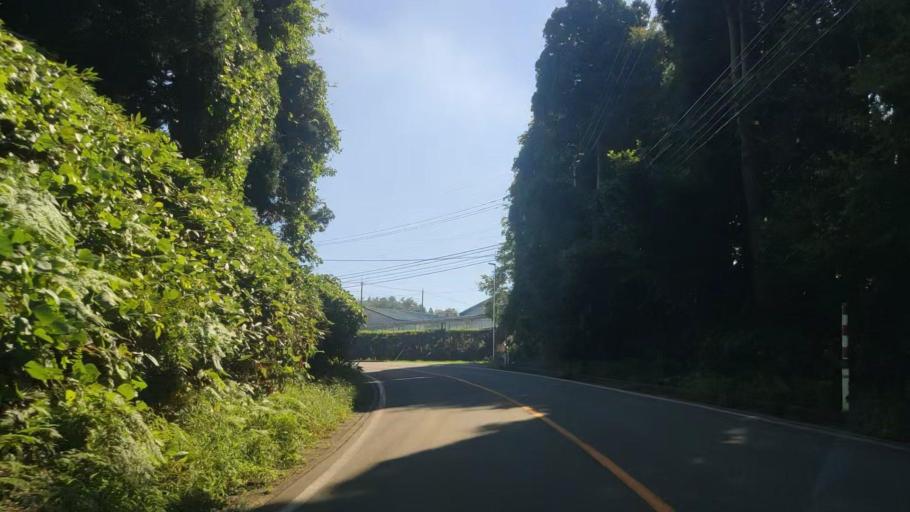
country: JP
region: Ishikawa
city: Nanao
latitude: 37.3457
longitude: 137.2280
